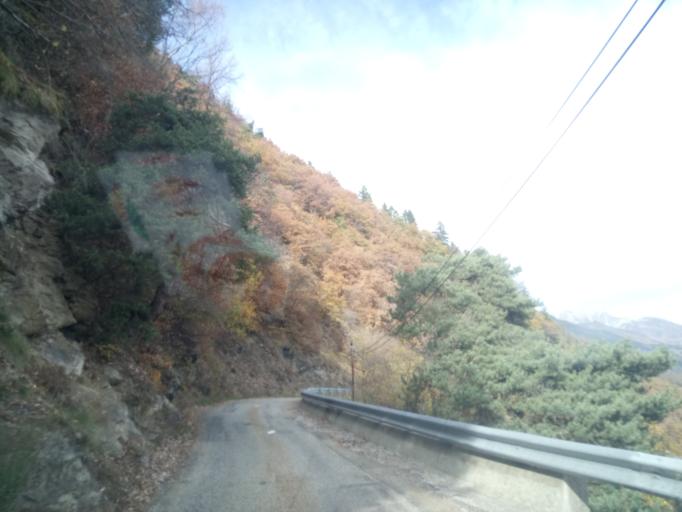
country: FR
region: Rhone-Alpes
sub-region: Departement de la Savoie
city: La Chambre
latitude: 45.3737
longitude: 6.3062
